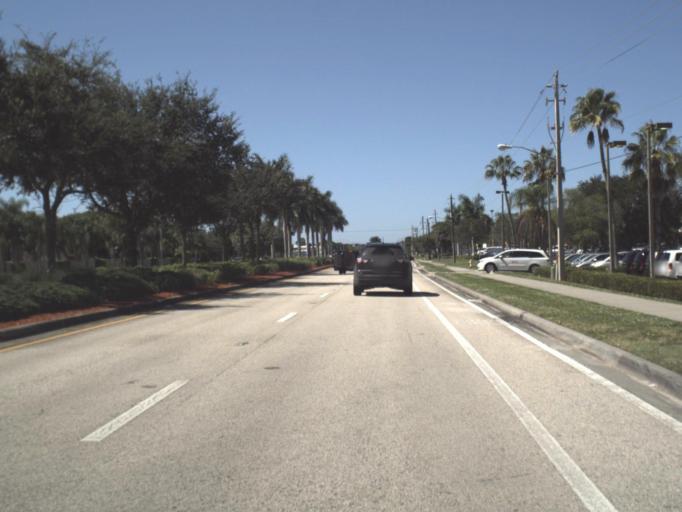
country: US
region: Florida
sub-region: Collier County
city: Naples
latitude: 26.1387
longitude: -81.7626
